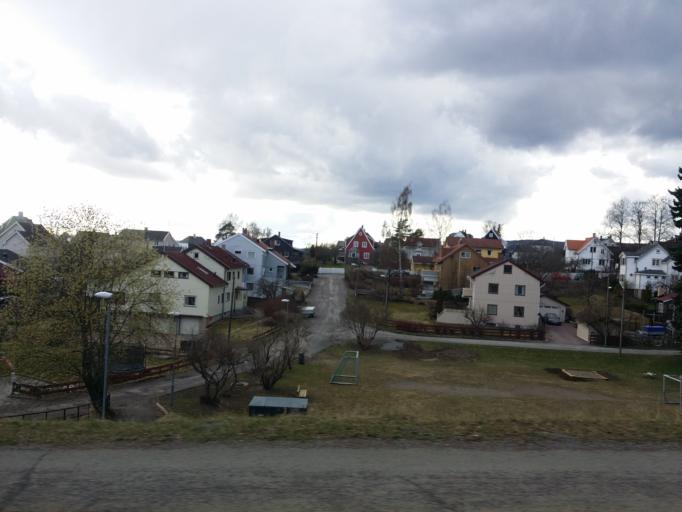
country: NO
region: Oslo
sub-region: Oslo
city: Oslo
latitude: 59.9487
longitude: 10.7899
